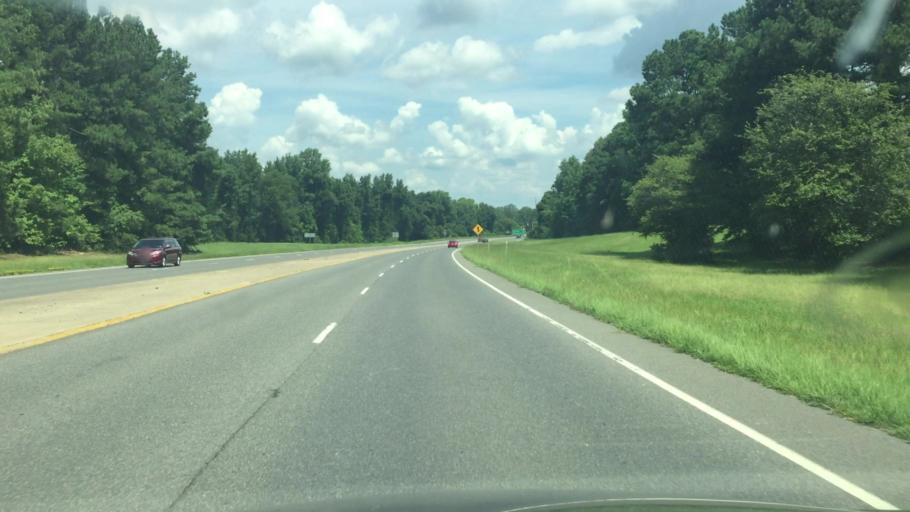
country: US
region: North Carolina
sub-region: Richmond County
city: Rockingham
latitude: 34.9322
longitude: -79.7805
